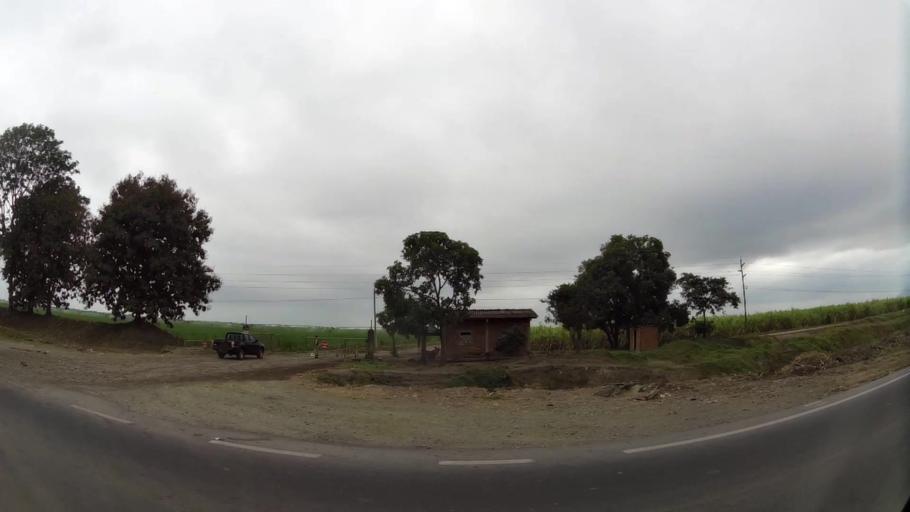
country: EC
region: Guayas
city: Naranjito
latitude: -2.3310
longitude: -79.6358
